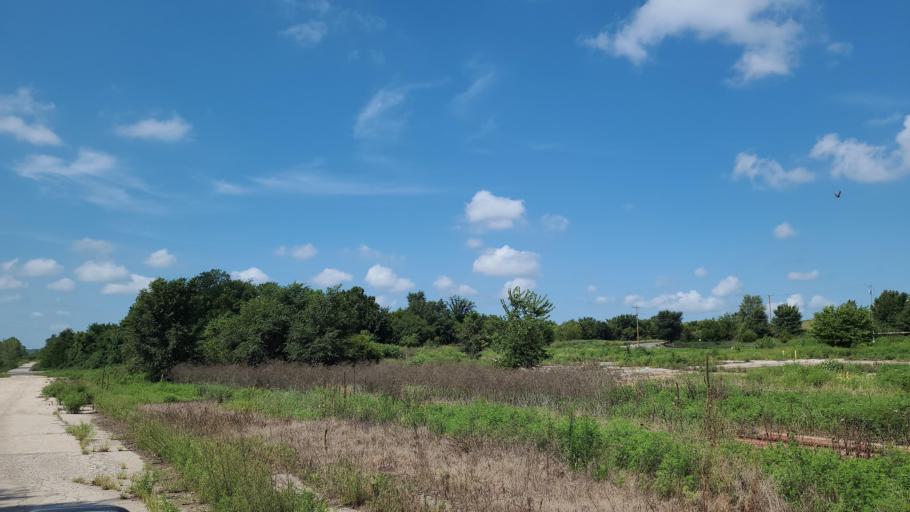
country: US
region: Kansas
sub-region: Douglas County
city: Lawrence
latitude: 38.9519
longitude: -95.1962
